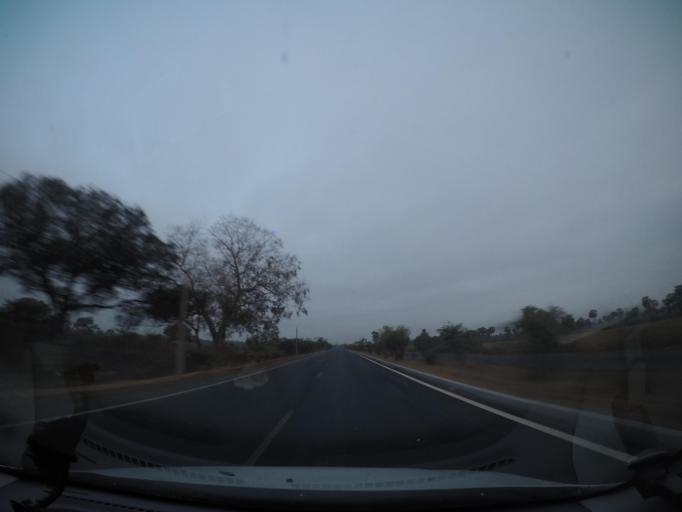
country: IN
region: Andhra Pradesh
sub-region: West Godavari
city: Tadepallegudem
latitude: 16.8100
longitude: 81.3369
